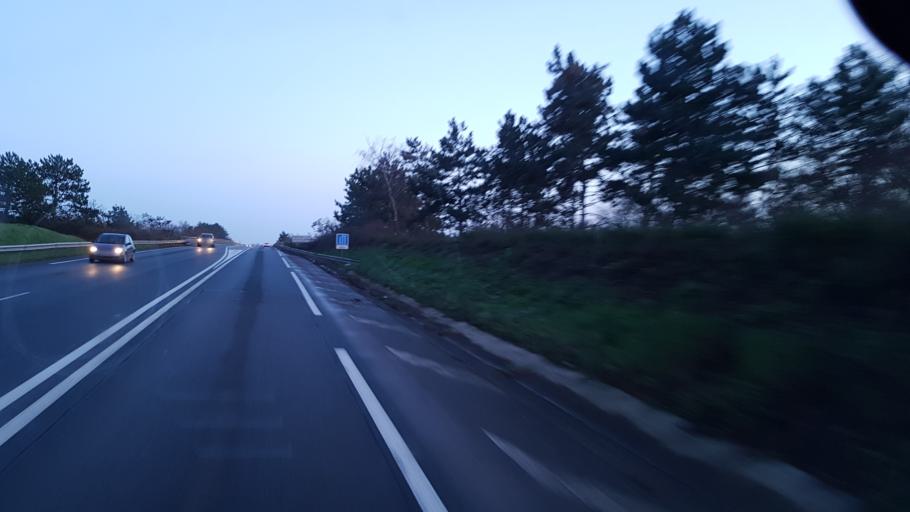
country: FR
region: Nord-Pas-de-Calais
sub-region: Departement du Nord
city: Lambres-lez-Douai
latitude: 50.3500
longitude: 3.0618
